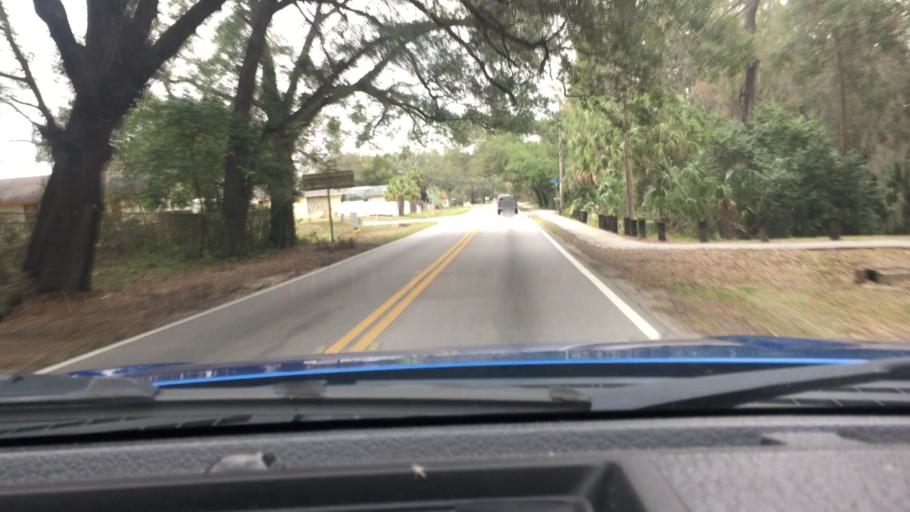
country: US
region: Florida
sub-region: Hillsborough County
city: Mango
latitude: 27.9612
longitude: -82.3104
